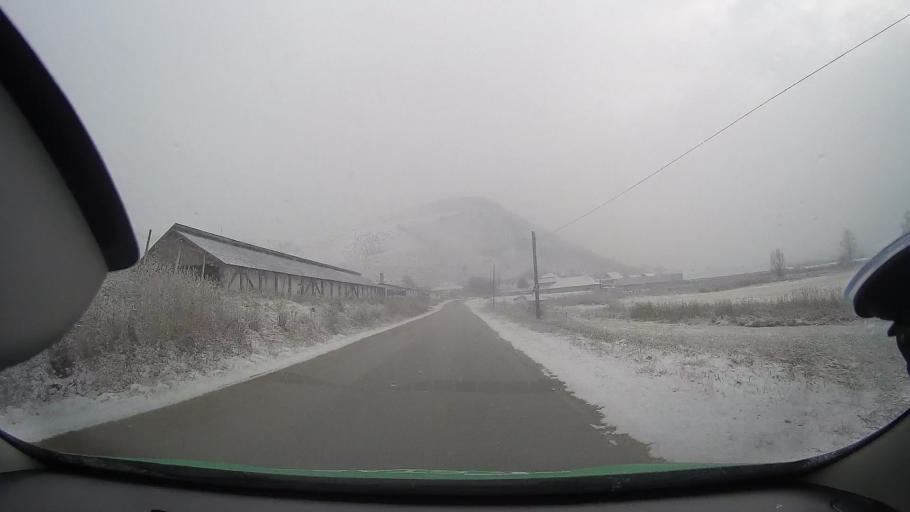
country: RO
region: Alba
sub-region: Comuna Lopadea Noua
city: Lopadea Noua
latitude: 46.2990
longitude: 23.8107
